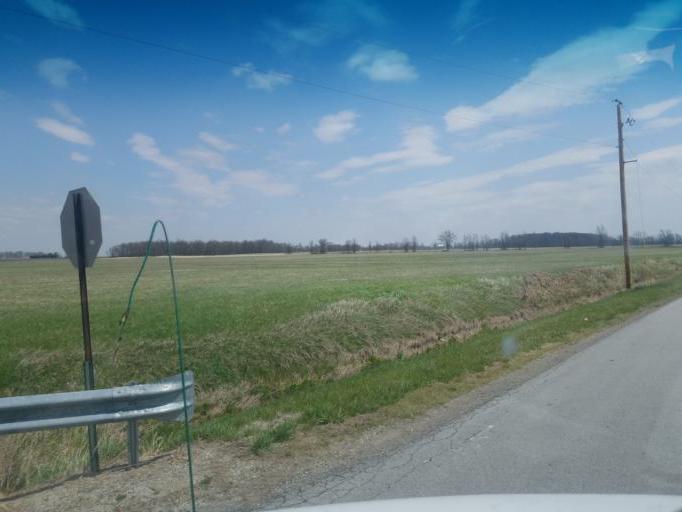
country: US
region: Ohio
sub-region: Hardin County
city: Forest
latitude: 40.7744
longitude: -83.4966
